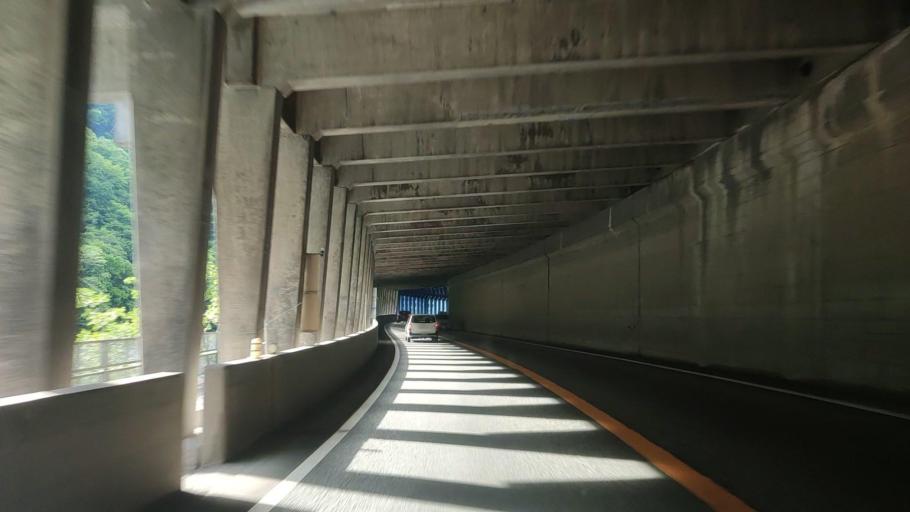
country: JP
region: Toyama
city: Yatsuomachi-higashikumisaka
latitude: 36.4167
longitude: 137.2894
